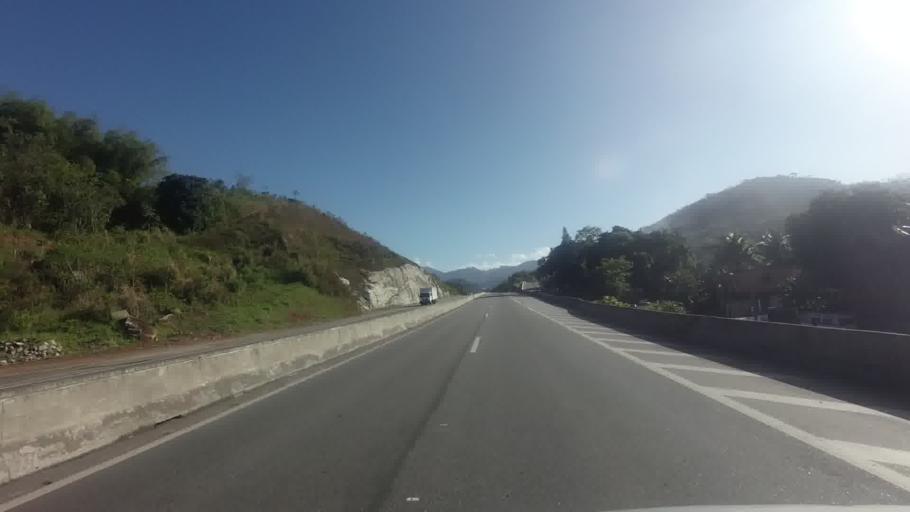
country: BR
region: Rio de Janeiro
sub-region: Petropolis
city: Petropolis
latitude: -22.6048
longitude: -43.2847
